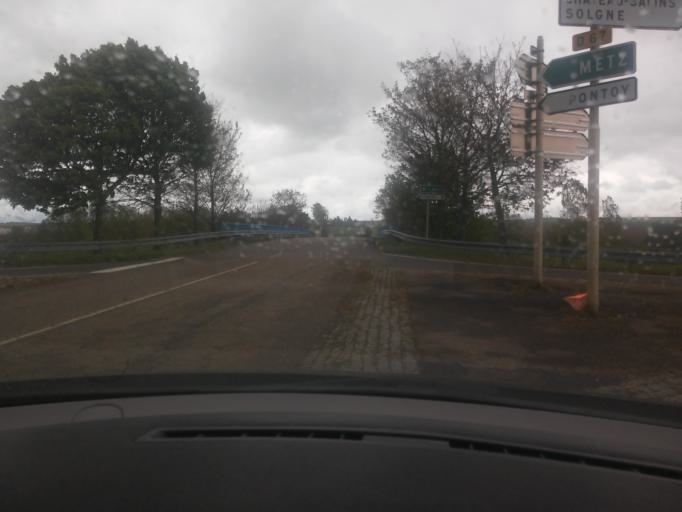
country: FR
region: Lorraine
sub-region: Departement de la Moselle
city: Mecleuves
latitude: 49.0139
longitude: 6.2694
